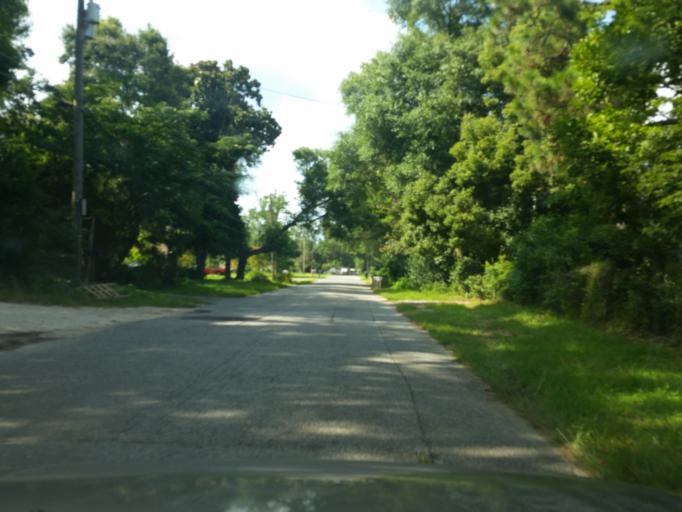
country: US
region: Florida
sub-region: Escambia County
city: Ferry Pass
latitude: 30.4967
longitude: -87.2143
